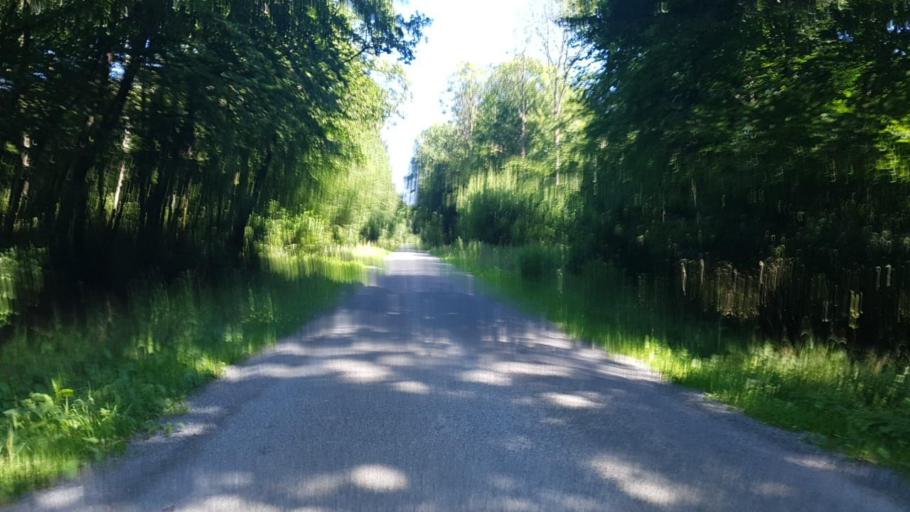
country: BE
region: Wallonia
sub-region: Province du Hainaut
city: Momignies
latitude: 50.0310
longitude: 4.2007
